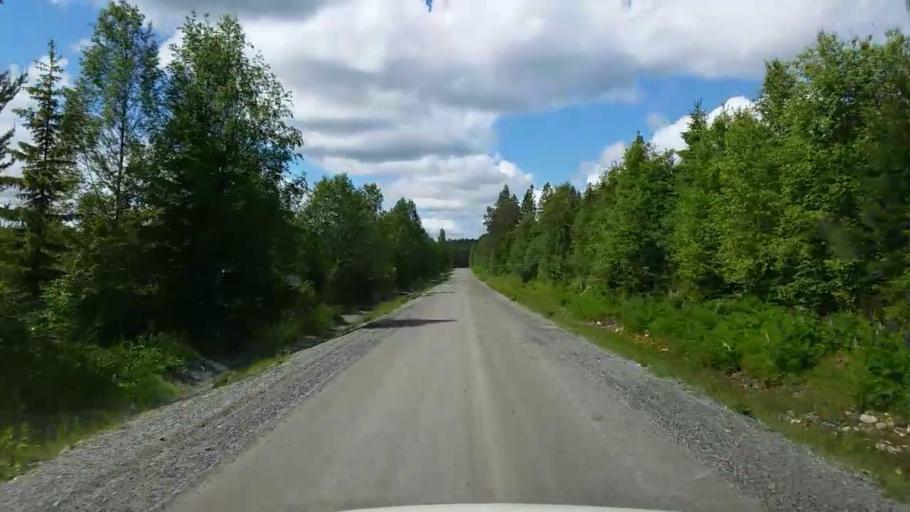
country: SE
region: Gaevleborg
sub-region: Bollnas Kommun
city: Vittsjo
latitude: 61.0896
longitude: 16.1847
